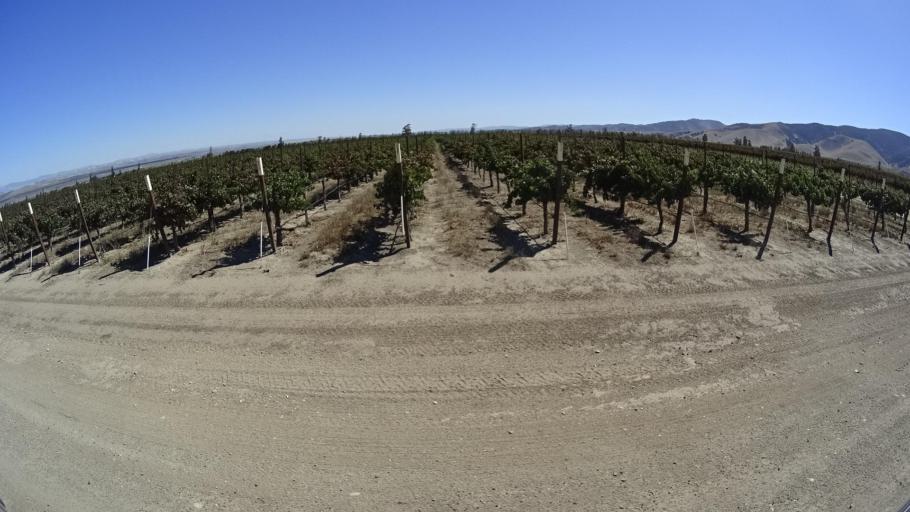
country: US
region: California
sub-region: Monterey County
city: Greenfield
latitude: 36.2661
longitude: -121.2047
